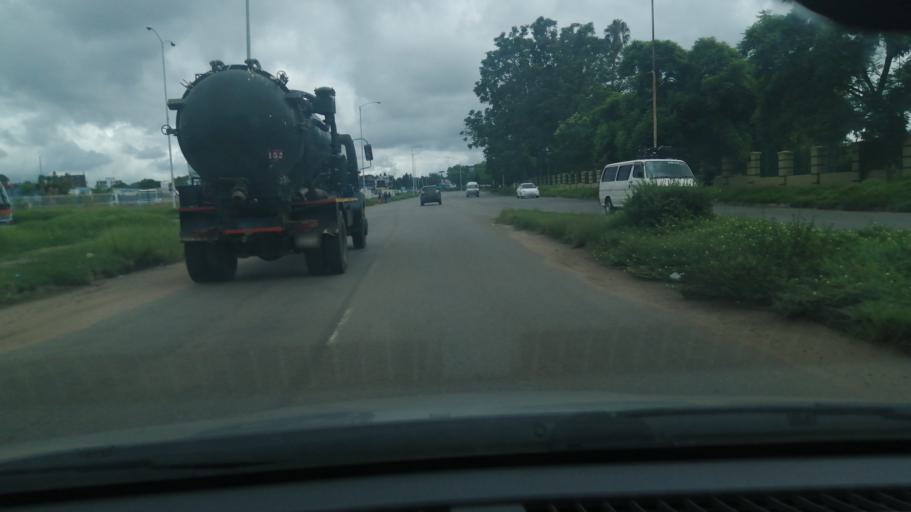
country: ZW
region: Harare
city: Harare
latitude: -17.8269
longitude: 31.0609
